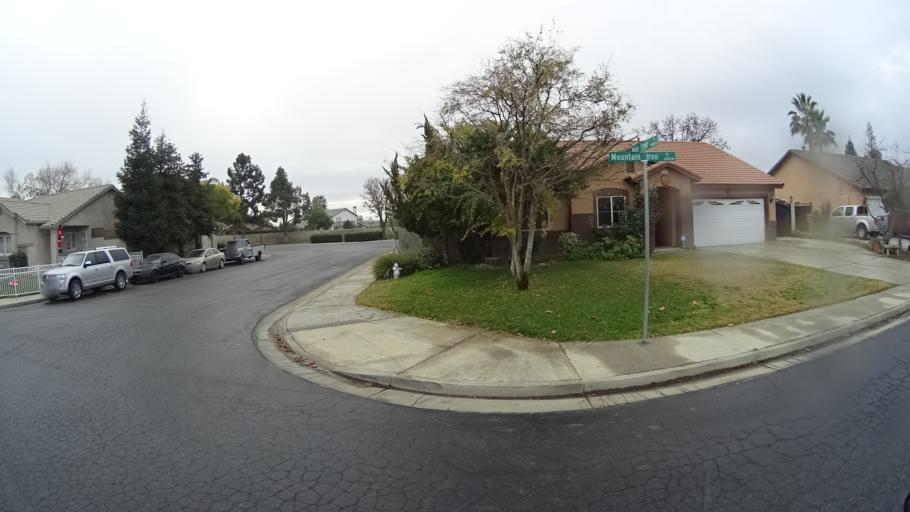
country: US
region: California
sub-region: Kern County
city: Greenfield
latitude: 35.3039
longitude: -119.0774
